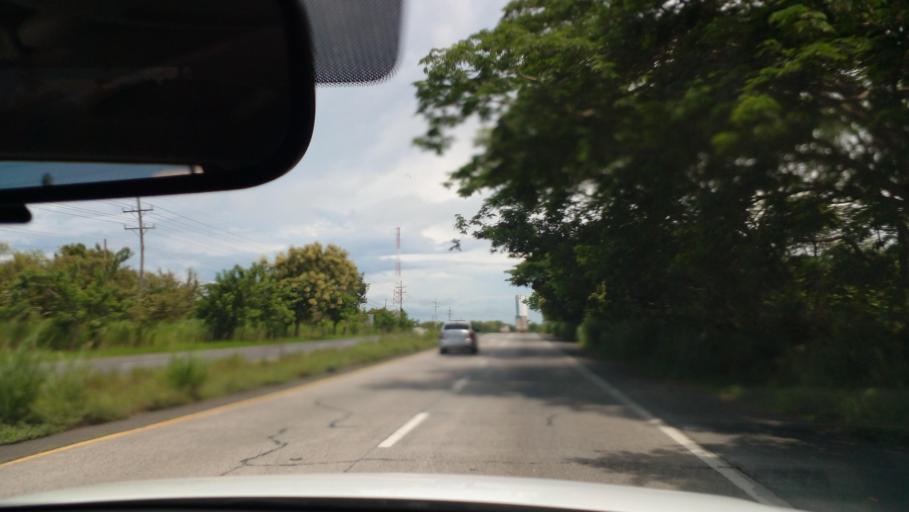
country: PA
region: Panama
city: Nueva Gorgona
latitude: 8.4830
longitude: -79.9583
